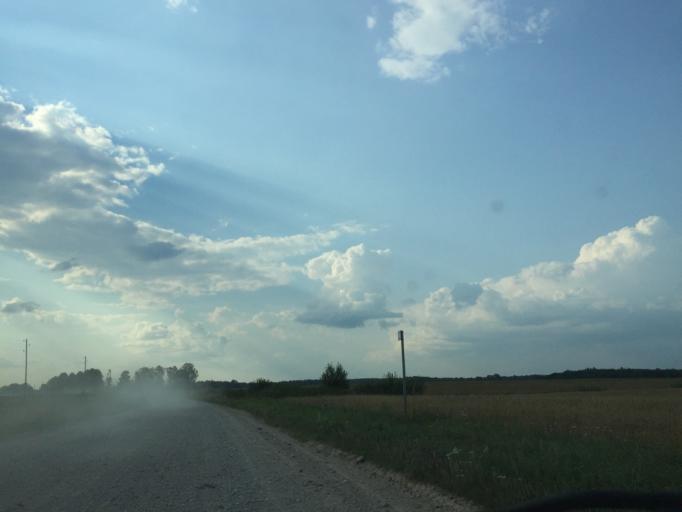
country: LT
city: Zagare
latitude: 56.4710
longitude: 23.1539
